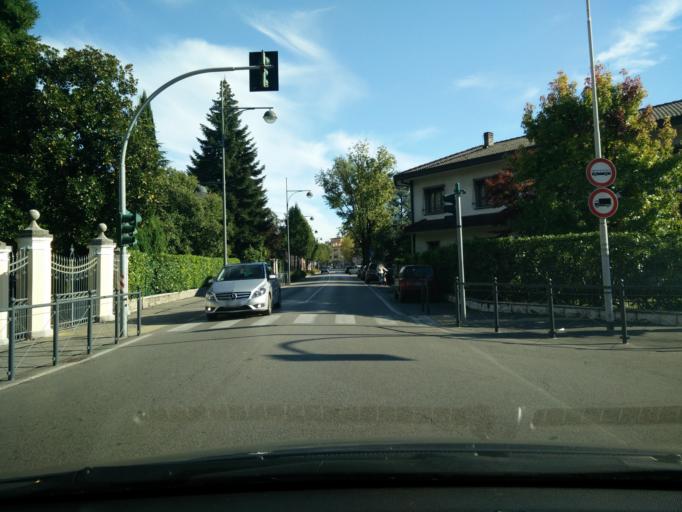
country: IT
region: Veneto
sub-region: Provincia di Venezia
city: San Dona di Piave
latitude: 45.6336
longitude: 12.5641
